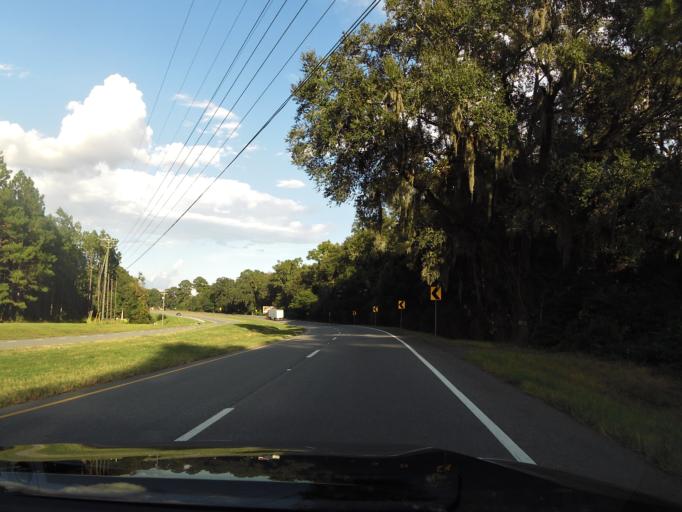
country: US
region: Georgia
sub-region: Lowndes County
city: Remerton
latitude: 30.7989
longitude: -83.3723
